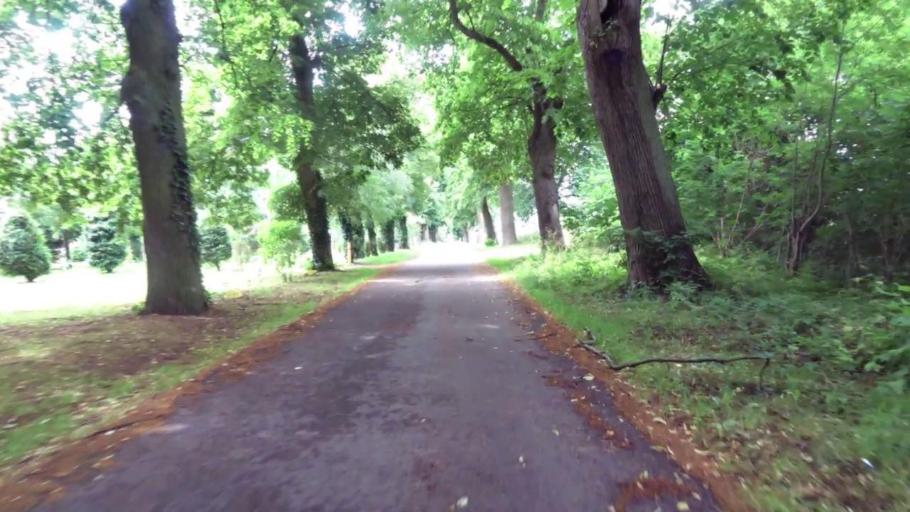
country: PL
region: West Pomeranian Voivodeship
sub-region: Powiat mysliborski
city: Mysliborz
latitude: 52.9755
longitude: 14.8870
